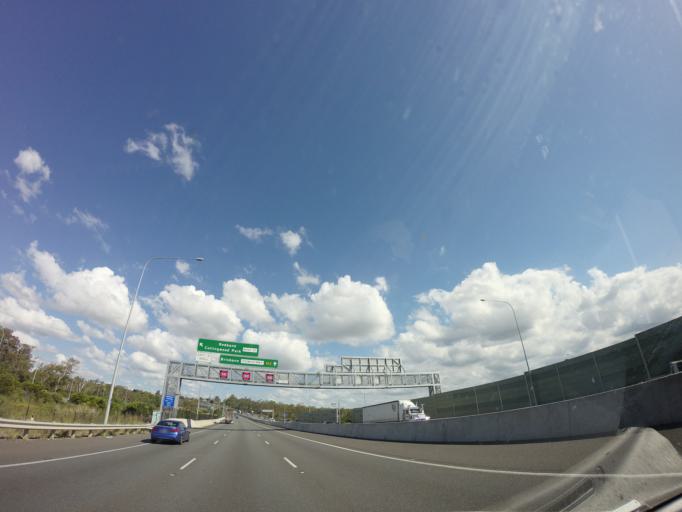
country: AU
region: Queensland
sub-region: Ipswich
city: Riverview
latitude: -27.6002
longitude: 152.8578
